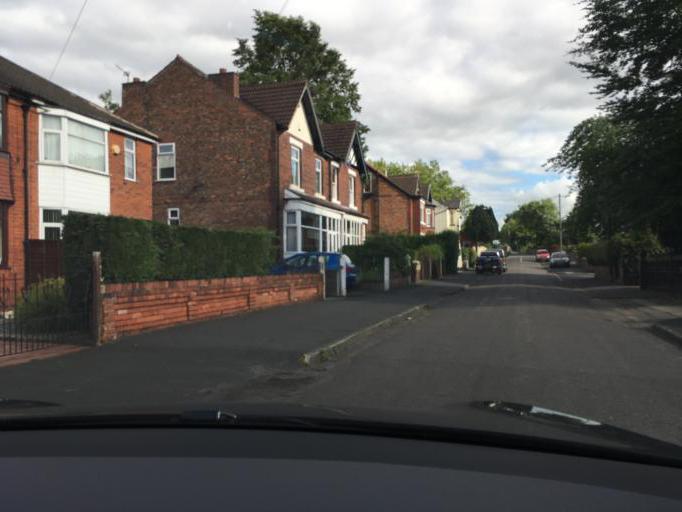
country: GB
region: England
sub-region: Trafford
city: Urmston
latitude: 53.4503
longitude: -2.3482
